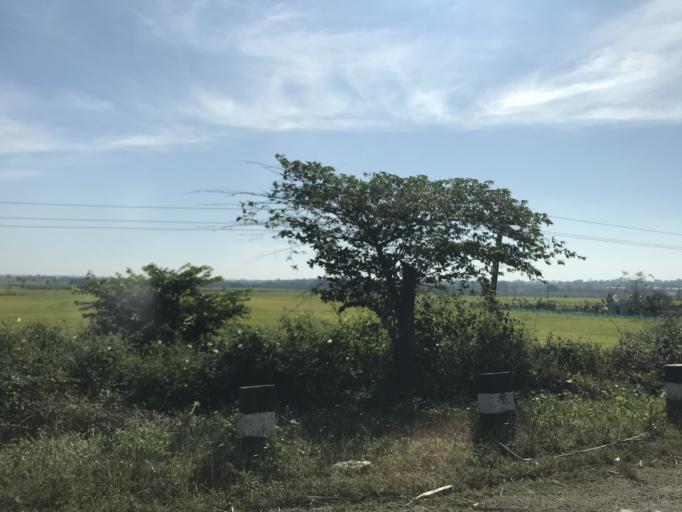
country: IN
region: Karnataka
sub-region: Mysore
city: Heggadadevankote
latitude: 12.1221
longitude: 76.4238
